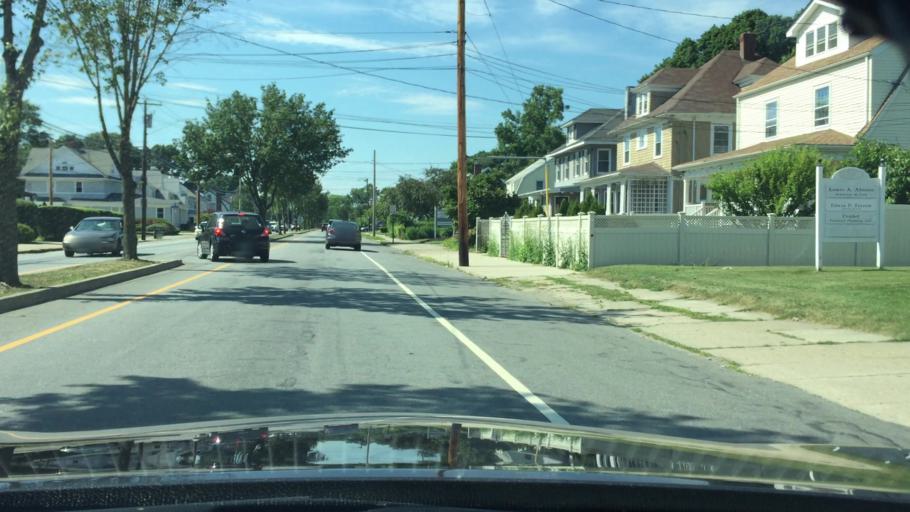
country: US
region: Connecticut
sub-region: Fairfield County
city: Trumbull
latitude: 41.2069
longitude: -73.2067
